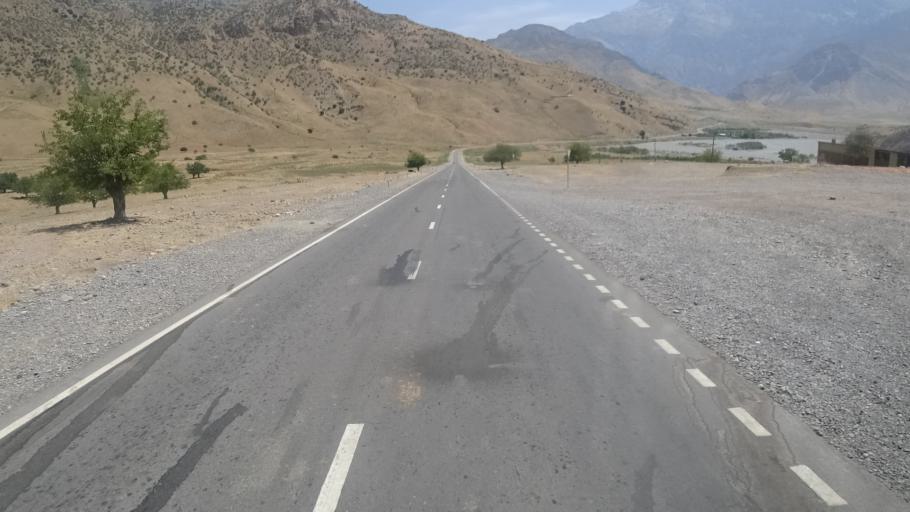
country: AF
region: Badakhshan
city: Deh Khwahan
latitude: 37.9475
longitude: 70.1720
